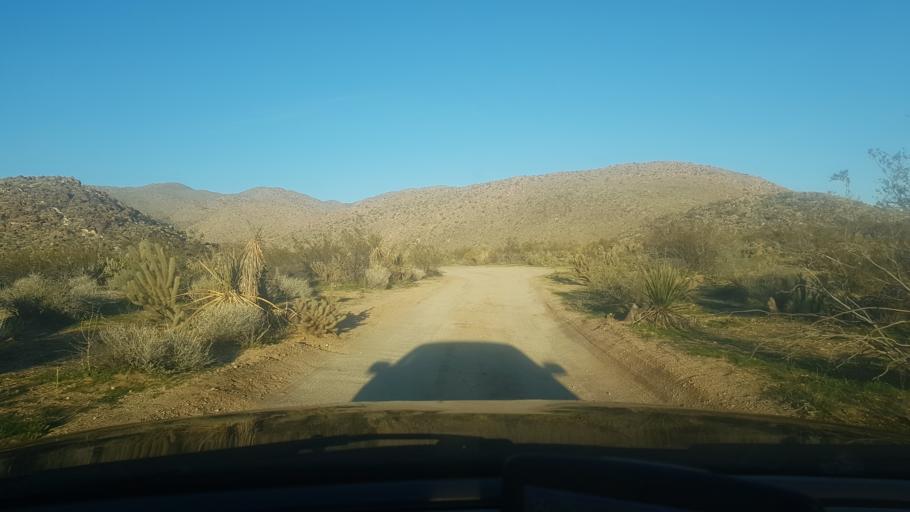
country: US
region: California
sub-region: San Diego County
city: Julian
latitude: 33.0076
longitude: -116.3823
